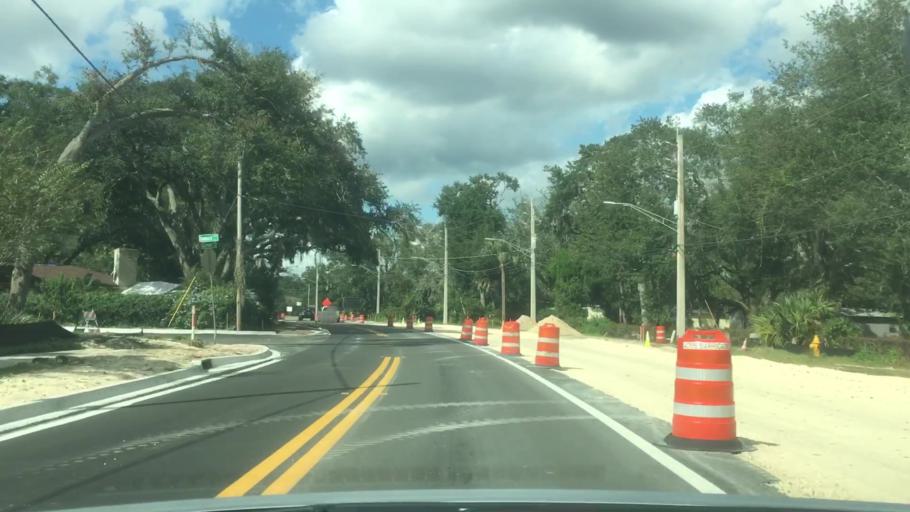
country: US
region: Florida
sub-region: Duval County
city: Atlantic Beach
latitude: 30.3556
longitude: -81.4614
